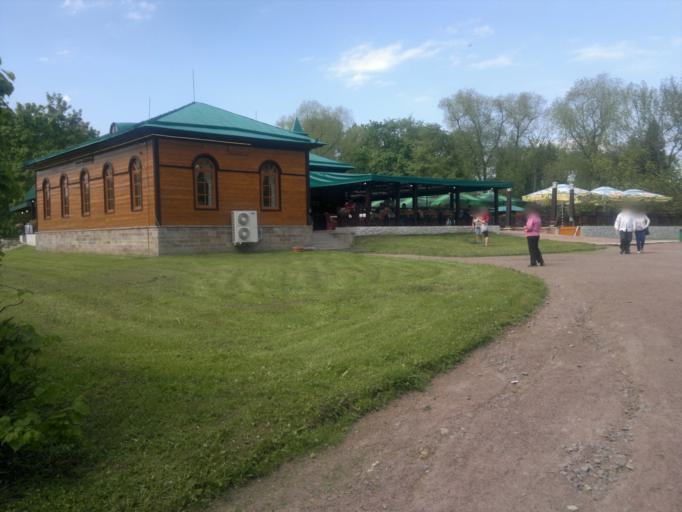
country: RU
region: St.-Petersburg
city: Peterhof
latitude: 59.8878
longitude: 29.9089
